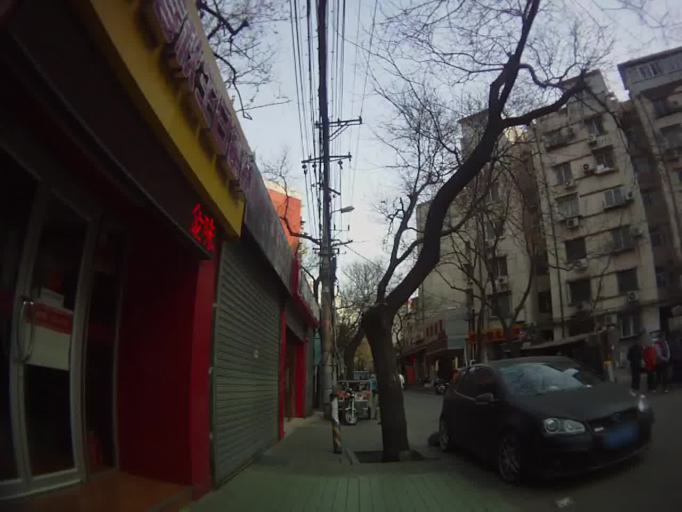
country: CN
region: Beijing
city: Chaowai
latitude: 39.9055
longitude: 116.4398
